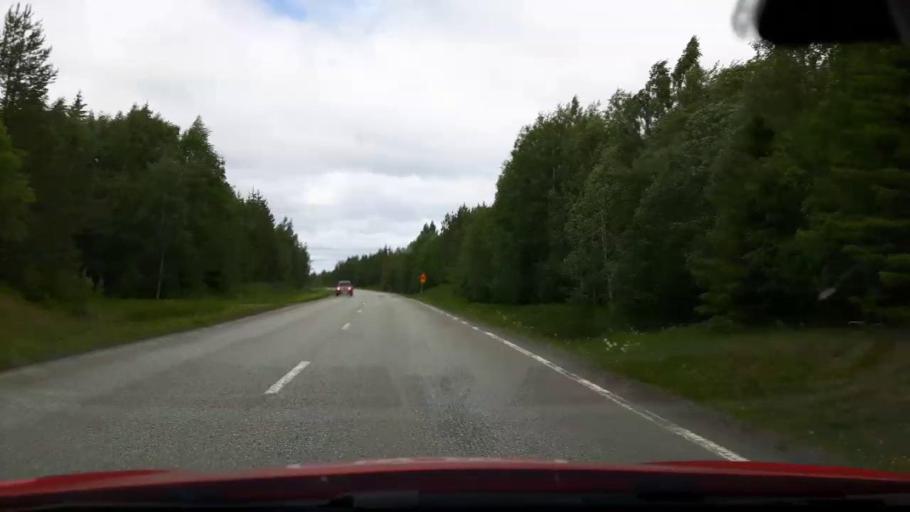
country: SE
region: Jaemtland
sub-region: Krokoms Kommun
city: Krokom
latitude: 63.3875
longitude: 14.5069
